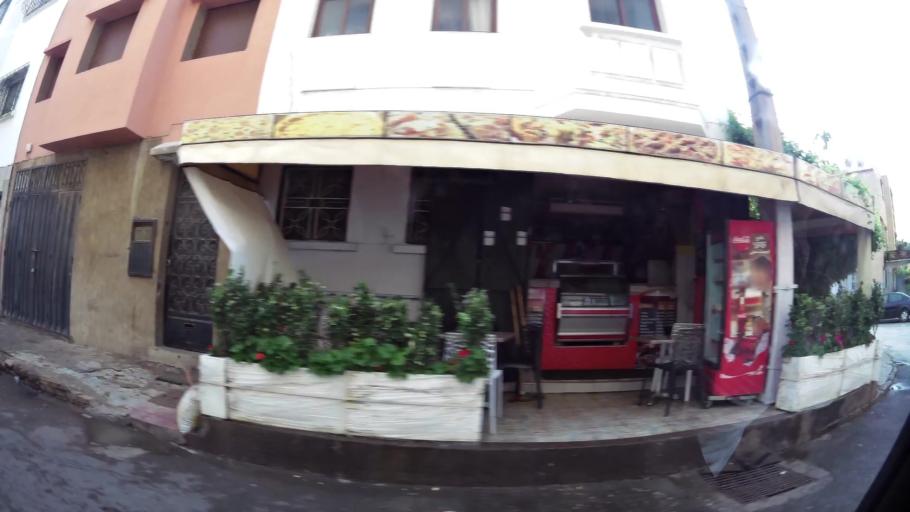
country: MA
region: Grand Casablanca
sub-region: Casablanca
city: Casablanca
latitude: 33.5651
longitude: -7.6723
